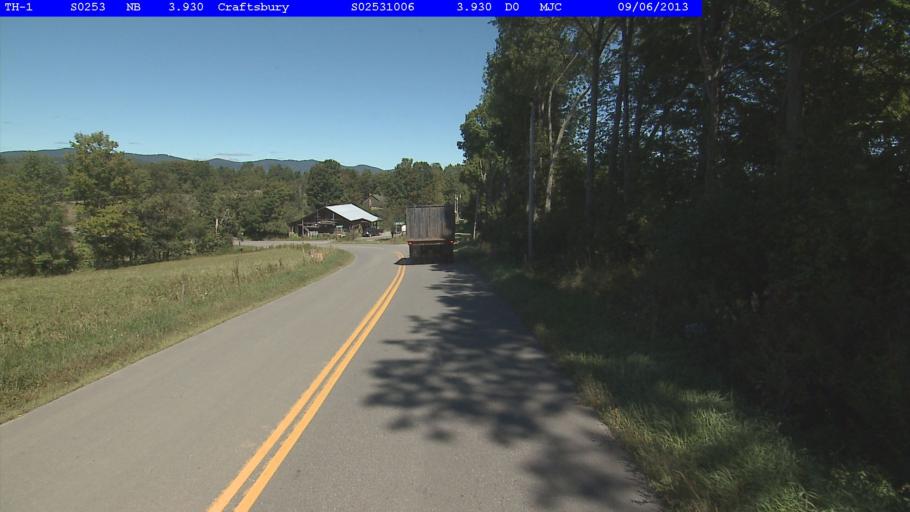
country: US
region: Vermont
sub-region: Caledonia County
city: Hardwick
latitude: 44.6648
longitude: -72.3835
